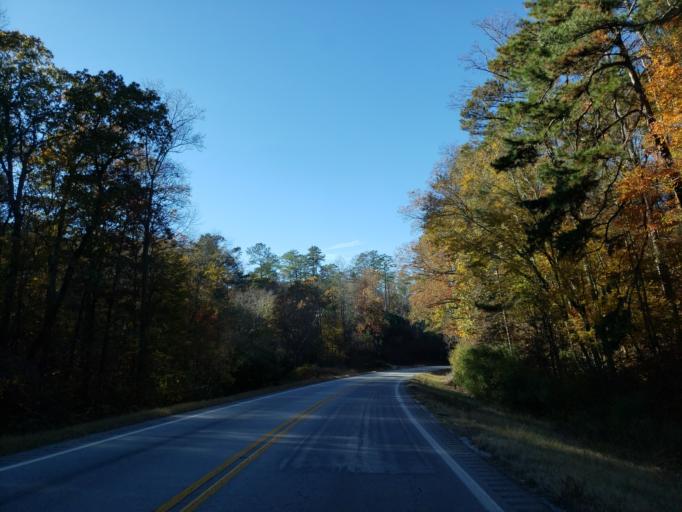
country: US
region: Alabama
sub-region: Calhoun County
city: Choccolocco
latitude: 33.5905
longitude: -85.6883
